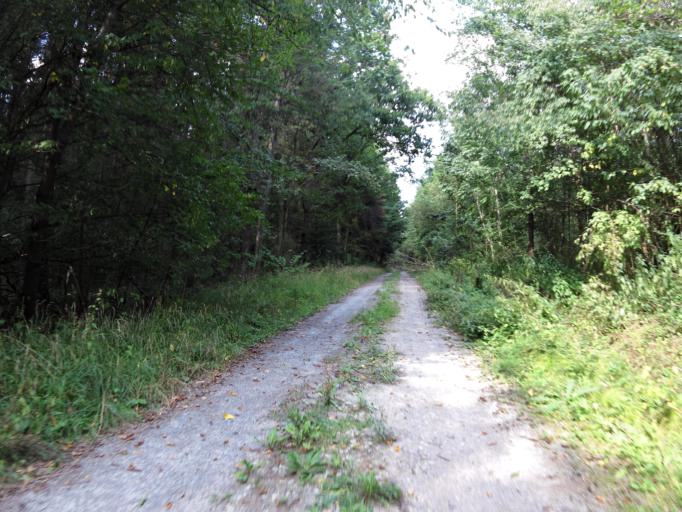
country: DE
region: Bavaria
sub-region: Regierungsbezirk Unterfranken
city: Kleinrinderfeld
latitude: 49.7021
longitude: 9.8084
